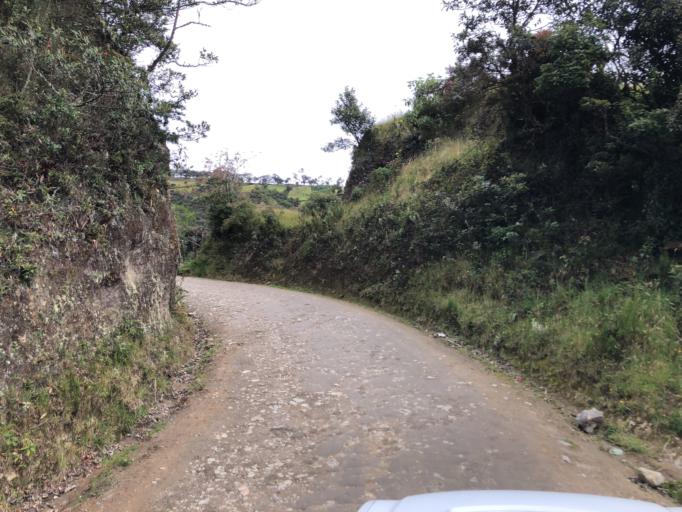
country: CO
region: Cauca
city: Totoro
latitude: 2.5001
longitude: -76.3575
